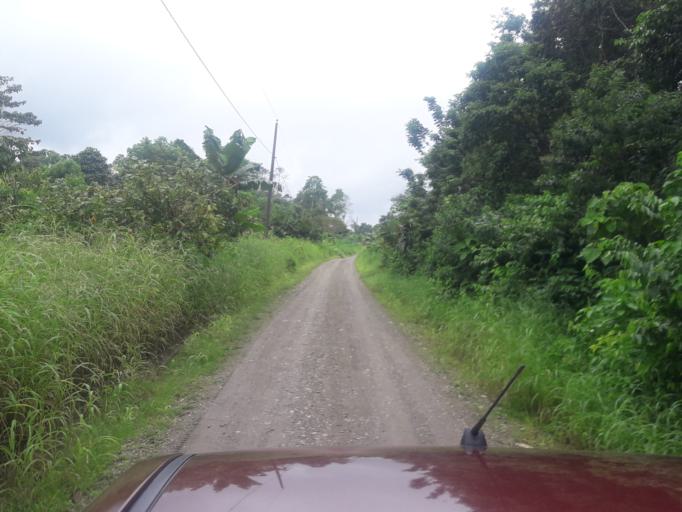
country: EC
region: Napo
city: Tena
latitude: -1.0258
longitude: -77.5989
